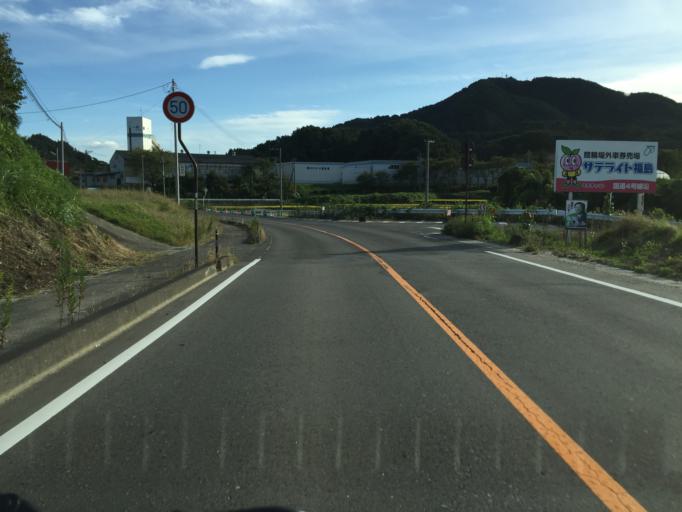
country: JP
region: Fukushima
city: Hobaramachi
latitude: 37.7670
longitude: 140.5954
